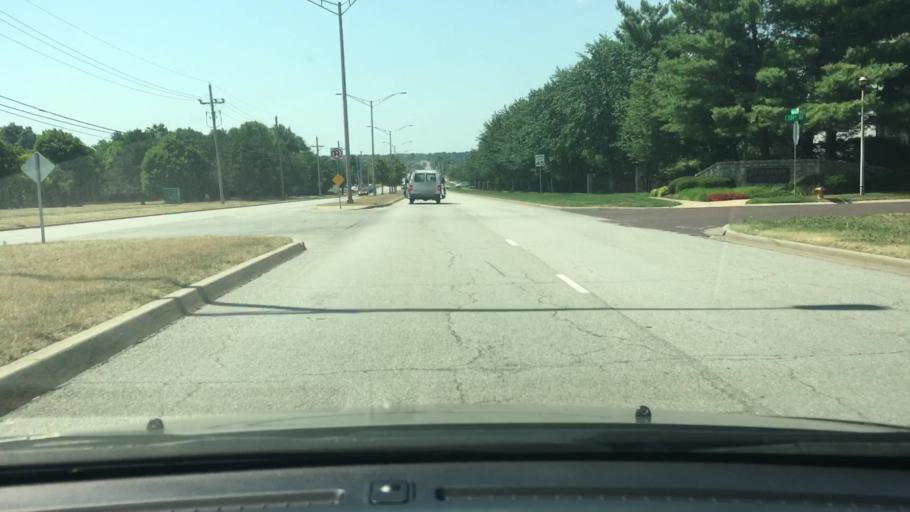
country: US
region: Kansas
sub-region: Johnson County
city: Lenexa
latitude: 38.8900
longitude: -94.7238
